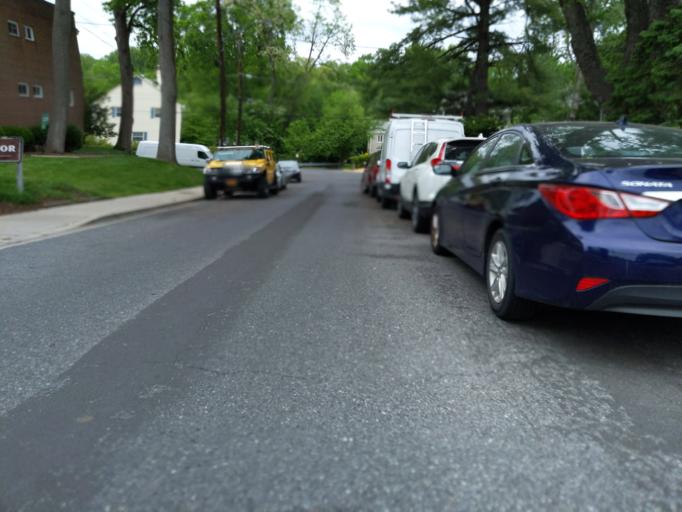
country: US
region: Maryland
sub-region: Montgomery County
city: Forest Glen
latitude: 39.0153
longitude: -77.0543
